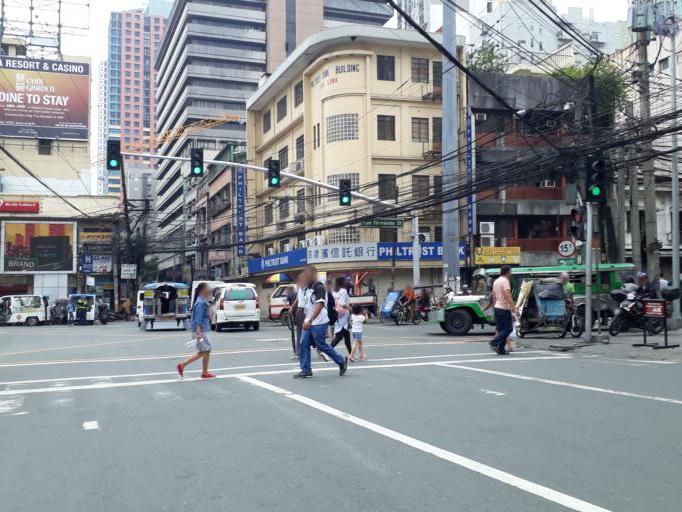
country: PH
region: Metro Manila
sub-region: City of Manila
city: Manila
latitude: 14.6001
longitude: 120.9739
